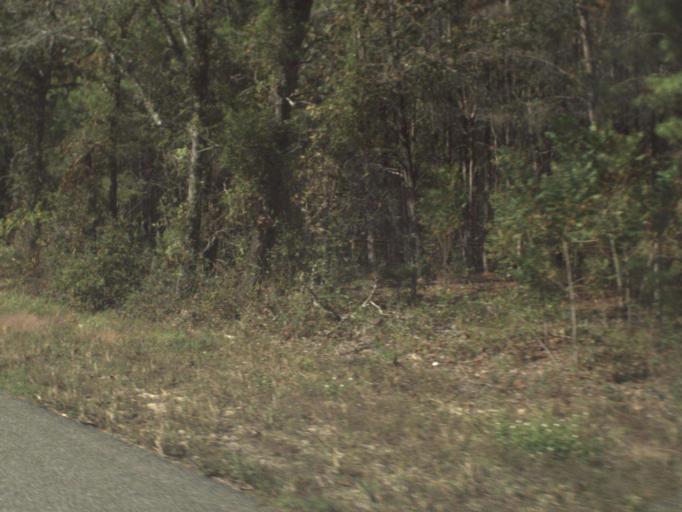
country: US
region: Florida
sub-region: Liberty County
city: Bristol
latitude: 30.4758
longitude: -84.9284
